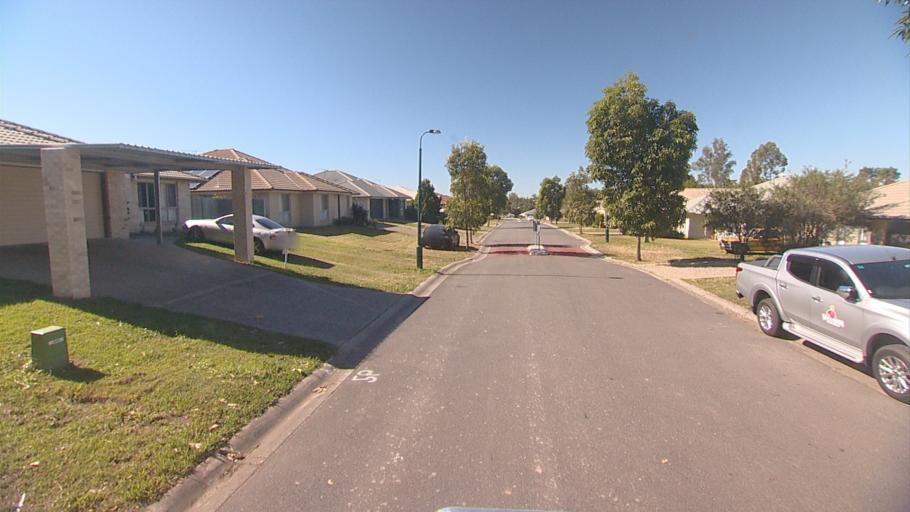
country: AU
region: Queensland
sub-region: Logan
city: Park Ridge South
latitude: -27.6713
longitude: 153.0206
